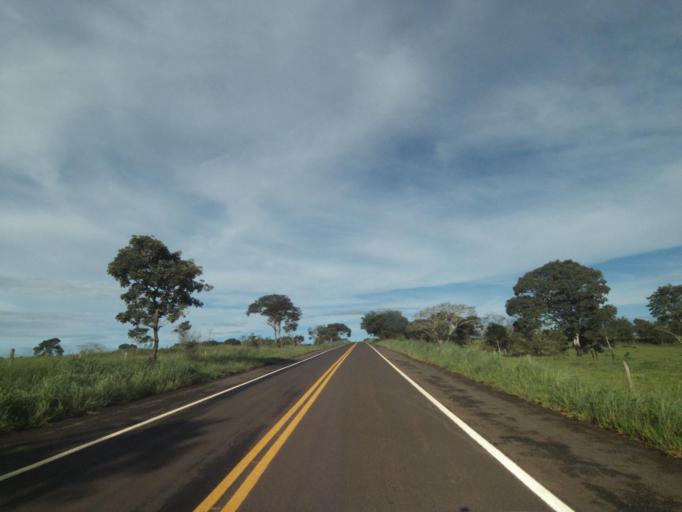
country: BR
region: Goias
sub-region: Itaberai
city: Itaberai
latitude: -15.9135
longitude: -49.5883
